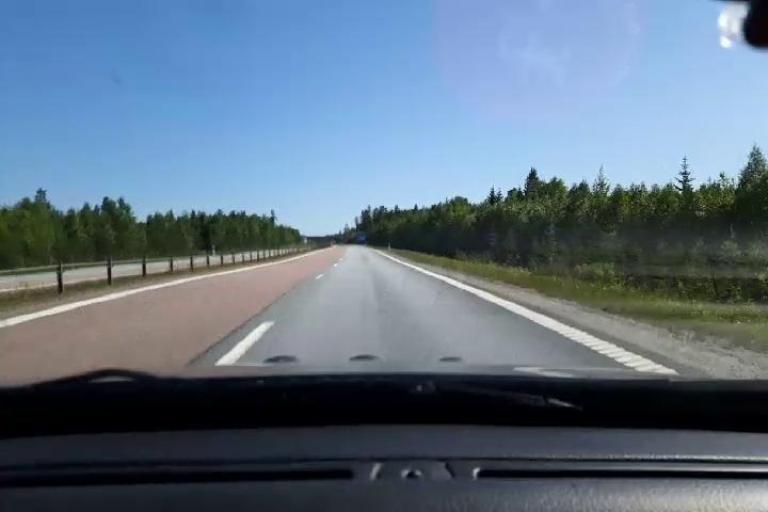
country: SE
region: Gaevleborg
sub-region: Hudiksvalls Kommun
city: Iggesund
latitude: 61.5261
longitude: 16.9729
